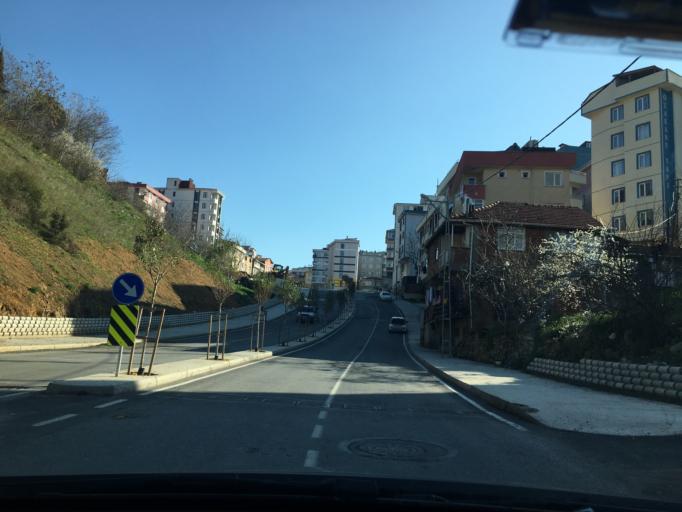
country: TR
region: Istanbul
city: Icmeler
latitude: 40.8708
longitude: 29.3021
